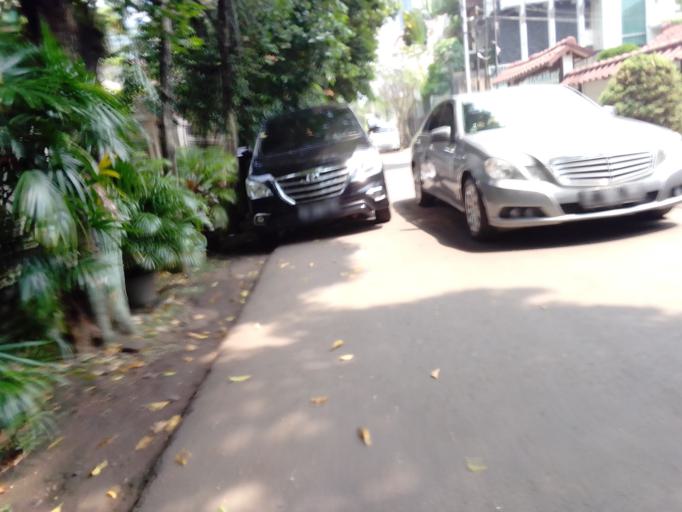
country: ID
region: Jakarta Raya
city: Jakarta
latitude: -6.2297
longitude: 106.8119
